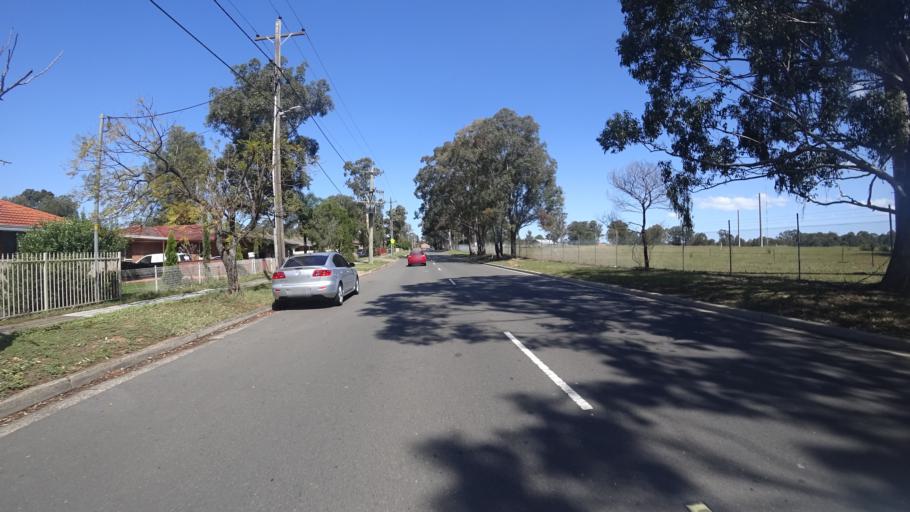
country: AU
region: New South Wales
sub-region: Liverpool
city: Miller
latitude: -33.9419
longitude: 150.8888
